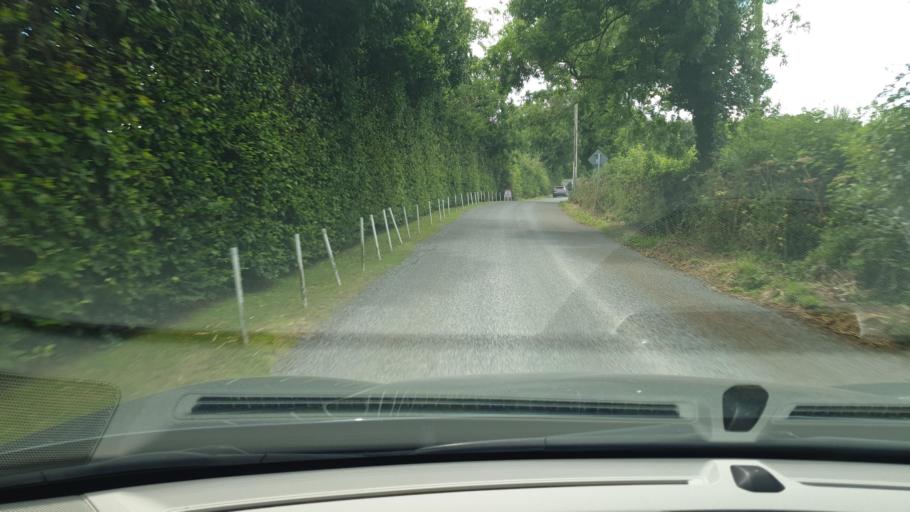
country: IE
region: Leinster
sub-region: An Mhi
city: Newtown Trim
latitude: 53.5435
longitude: -6.6957
